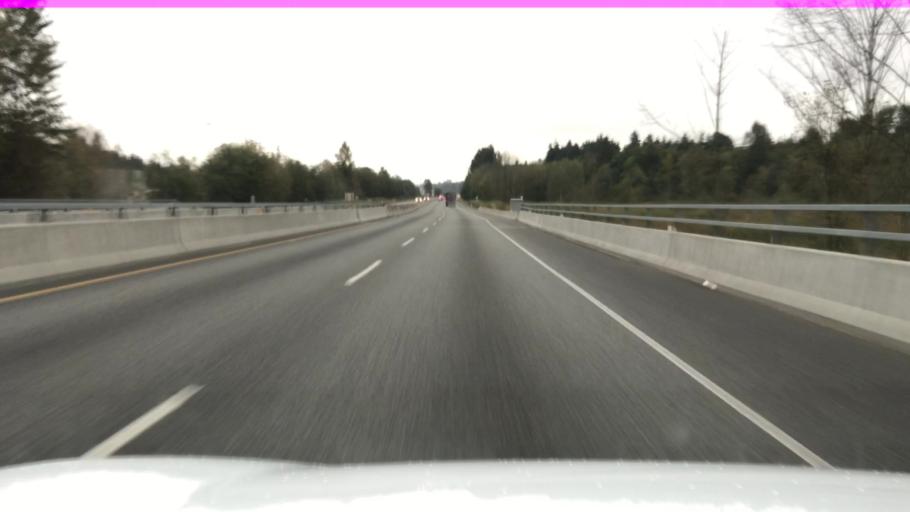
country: CA
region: British Columbia
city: Pitt Meadows
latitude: 49.2021
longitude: -122.7558
